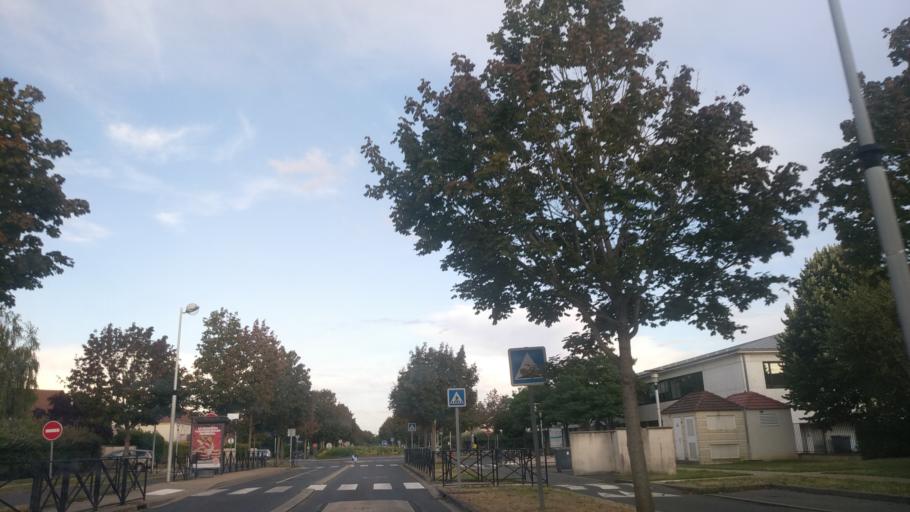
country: FR
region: Ile-de-France
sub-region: Departement de Seine-et-Marne
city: Lieusaint
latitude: 48.6374
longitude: 2.5517
